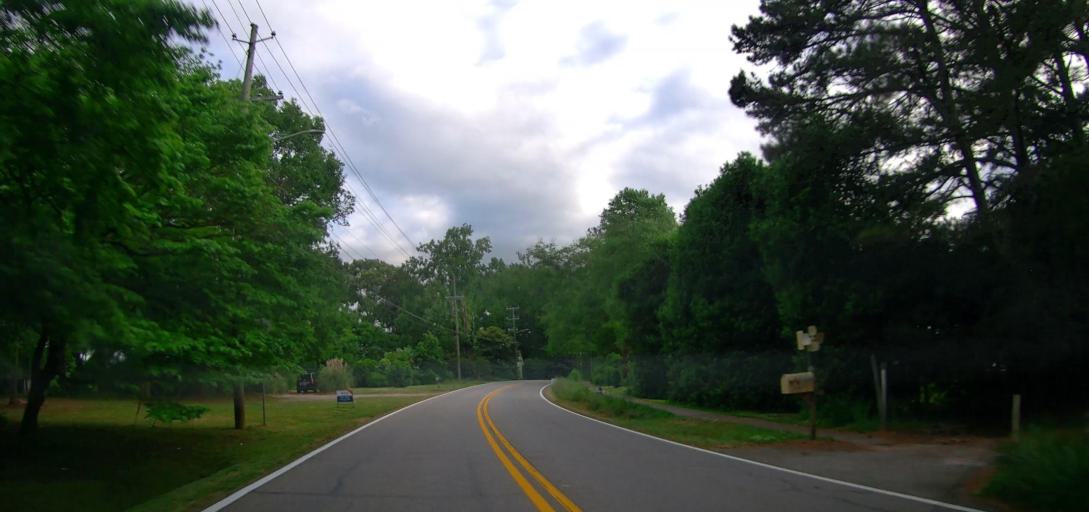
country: US
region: Georgia
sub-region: Oconee County
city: Watkinsville
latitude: 33.8572
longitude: -83.4072
